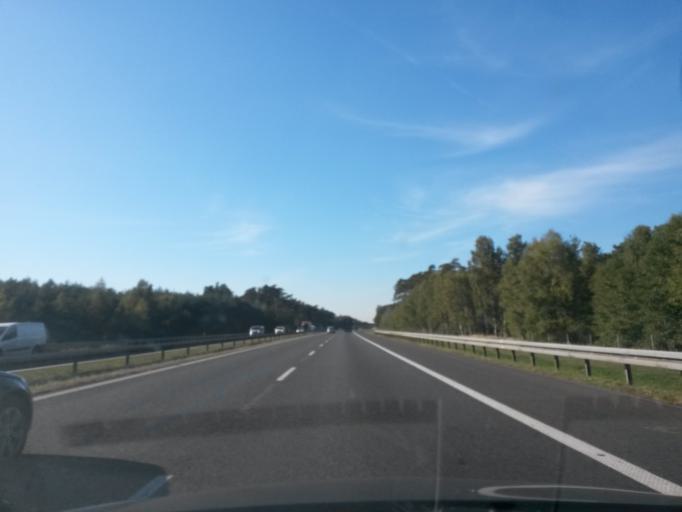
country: PL
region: Opole Voivodeship
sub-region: Powiat opolski
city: Niemodlin
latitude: 50.6673
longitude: 17.6779
